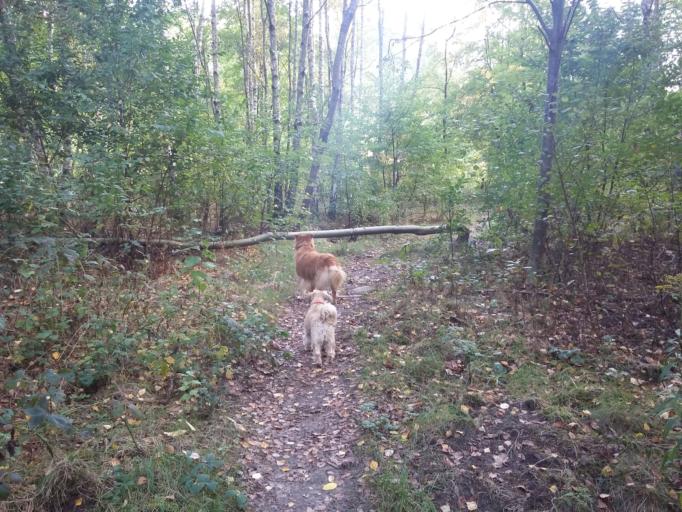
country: PL
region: Lodz Voivodeship
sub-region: Powiat pabianicki
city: Ksawerow
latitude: 51.7289
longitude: 19.4075
